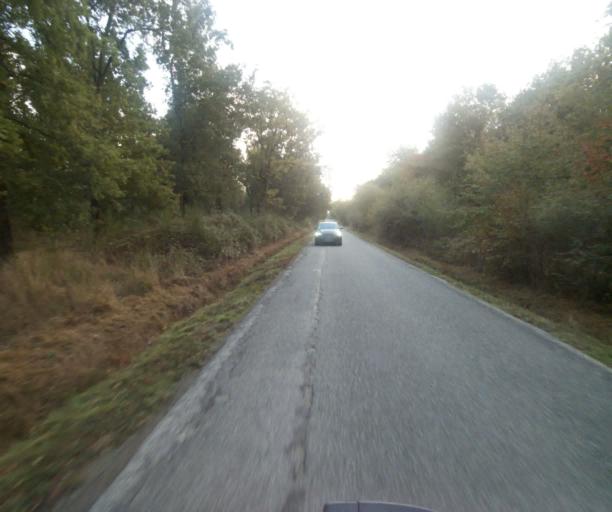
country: FR
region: Midi-Pyrenees
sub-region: Departement du Tarn-et-Garonne
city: Montech
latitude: 43.9429
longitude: 1.2846
